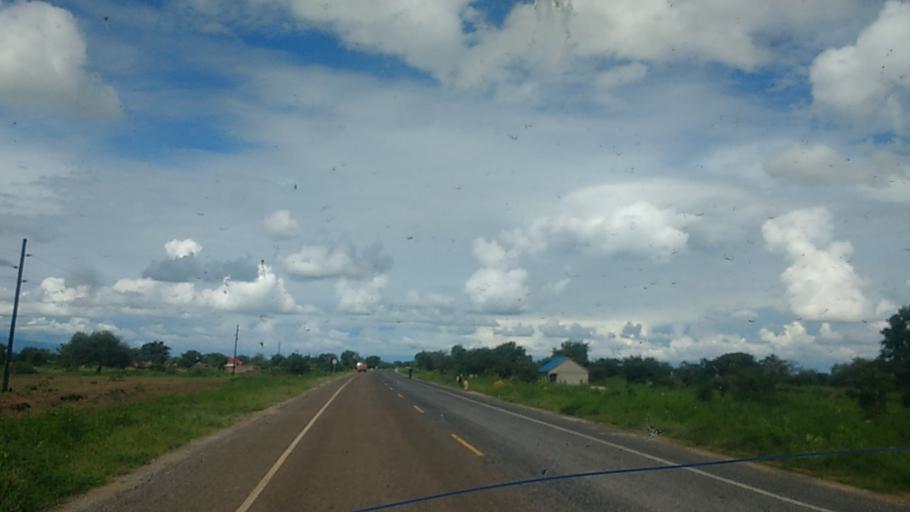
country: UG
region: Eastern Region
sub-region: Katakwi District
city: Katakwi
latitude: 1.9202
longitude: 33.9946
